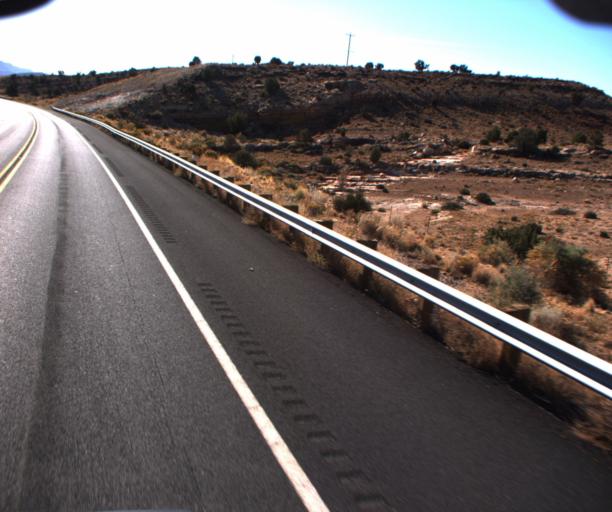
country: US
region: Arizona
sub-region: Coconino County
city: Tuba City
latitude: 36.3466
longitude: -111.5036
